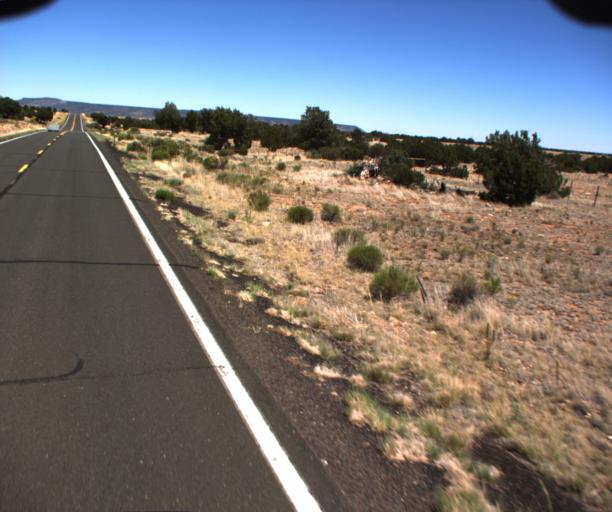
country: US
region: Arizona
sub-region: Coconino County
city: LeChee
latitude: 34.7597
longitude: -111.0234
